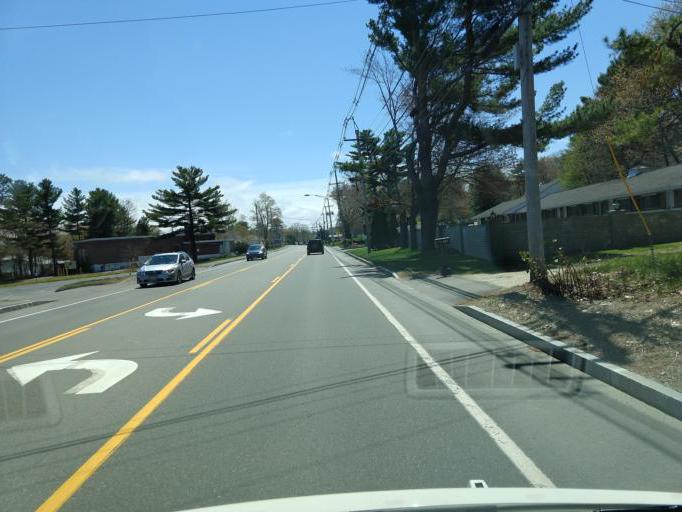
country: US
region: Maine
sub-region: York County
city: Ogunquit
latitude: 43.2667
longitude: -70.5975
